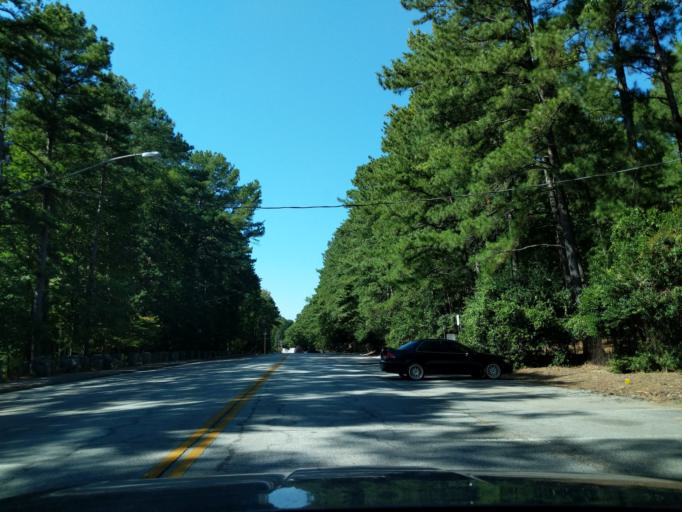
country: US
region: Georgia
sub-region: DeKalb County
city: Stone Mountain
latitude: 33.8150
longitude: -84.1482
